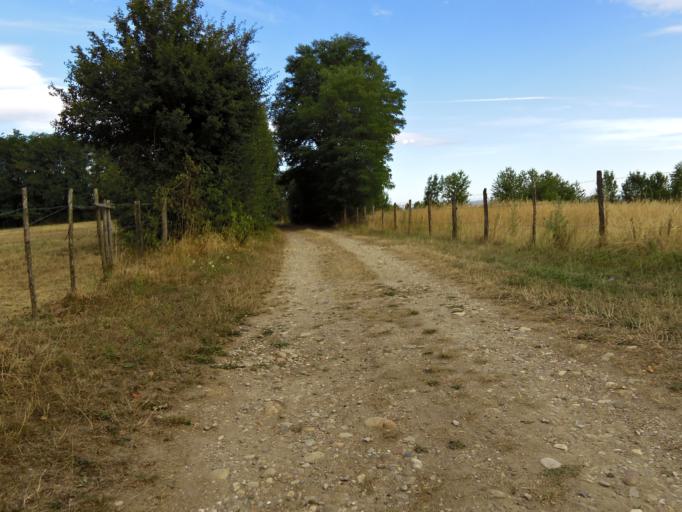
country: FR
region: Rhone-Alpes
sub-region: Departement de l'Ain
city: Meximieux
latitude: 45.9229
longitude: 5.1962
